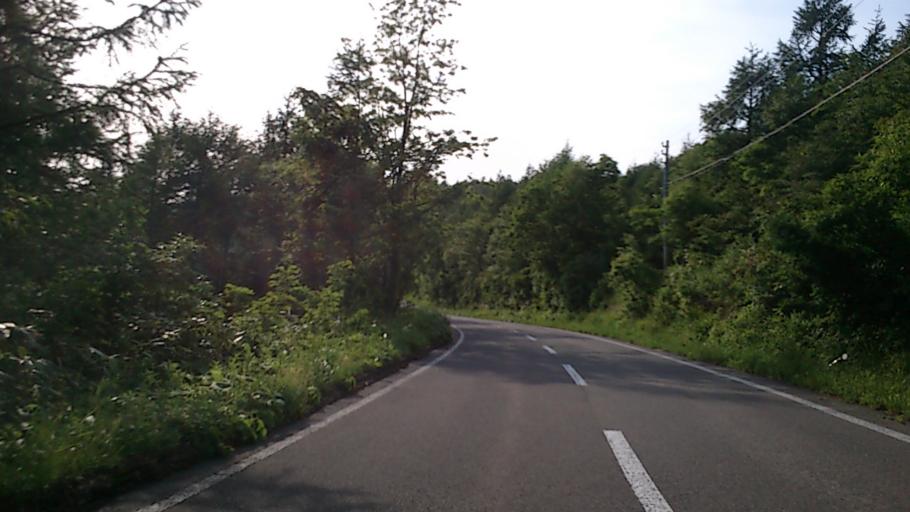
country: JP
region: Aomori
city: Aomori Shi
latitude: 40.6475
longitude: 140.7816
